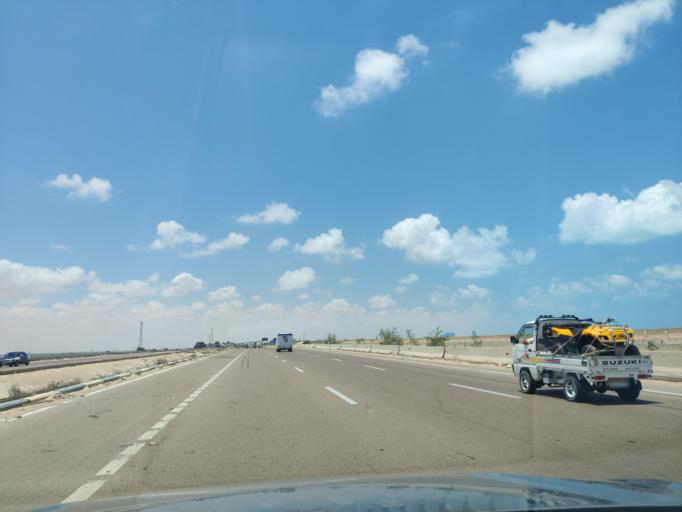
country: EG
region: Muhafazat Matruh
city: Al `Alamayn
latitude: 30.8126
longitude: 29.0788
